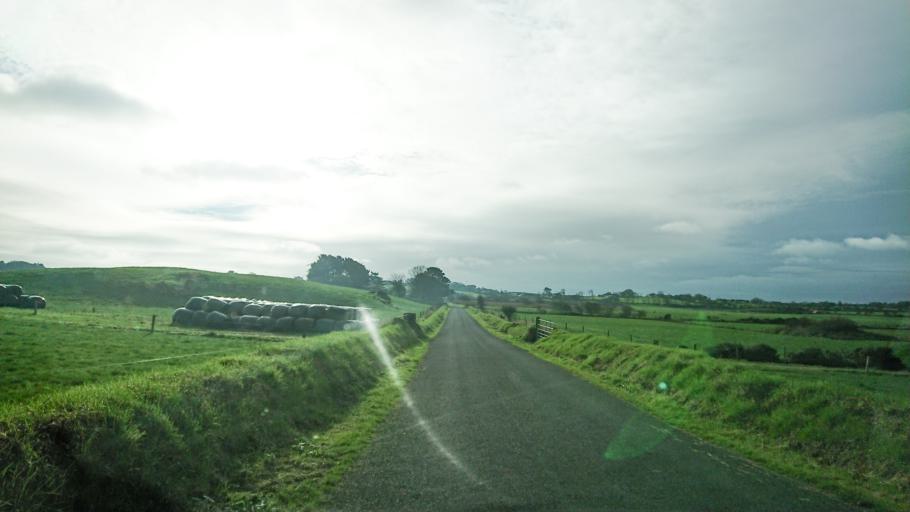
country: IE
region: Munster
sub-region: Waterford
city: Tra Mhor
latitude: 52.1642
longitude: -7.1874
